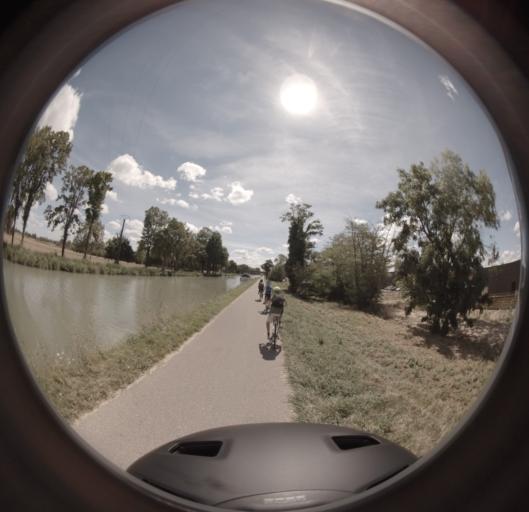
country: FR
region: Midi-Pyrenees
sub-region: Departement du Tarn-et-Garonne
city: Castelsarrasin
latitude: 44.0579
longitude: 1.1042
